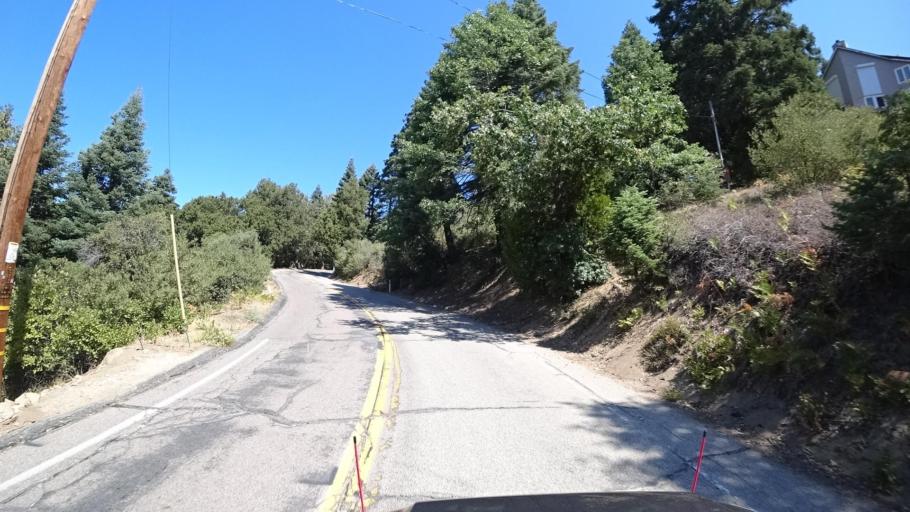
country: US
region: California
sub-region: Riverside County
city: Aguanga
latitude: 33.3144
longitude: -116.8610
